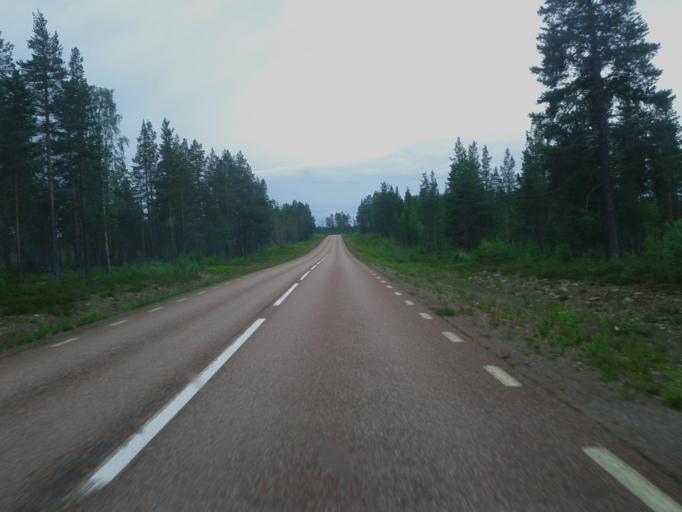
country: SE
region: Dalarna
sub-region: Alvdalens Kommun
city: AElvdalen
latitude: 61.4741
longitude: 13.4228
